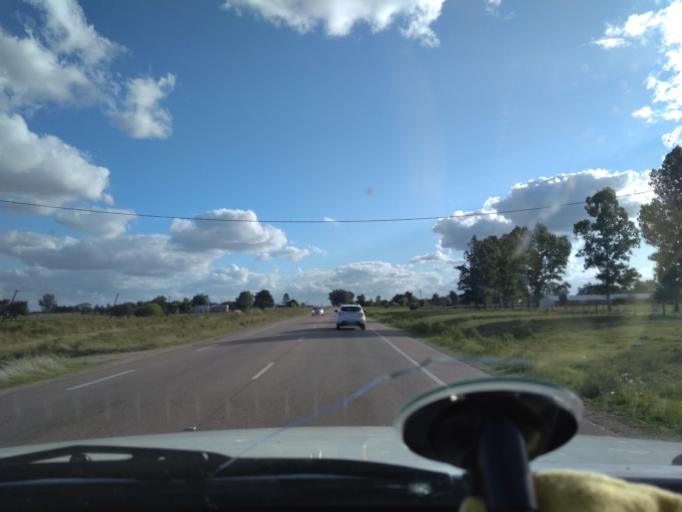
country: UY
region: Canelones
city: Tala
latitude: -34.3791
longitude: -55.7924
